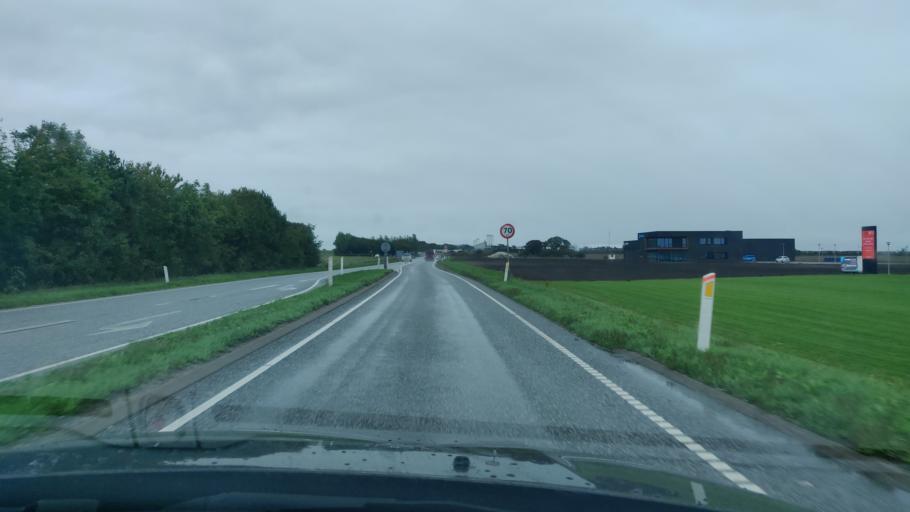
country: DK
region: North Denmark
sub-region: Thisted Kommune
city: Thisted
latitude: 56.9714
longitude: 8.7357
